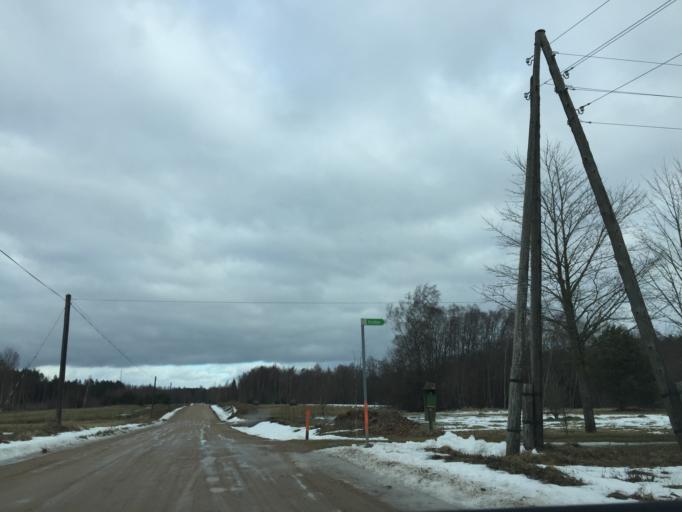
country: LV
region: Salacgrivas
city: Ainazi
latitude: 57.8523
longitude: 24.4899
